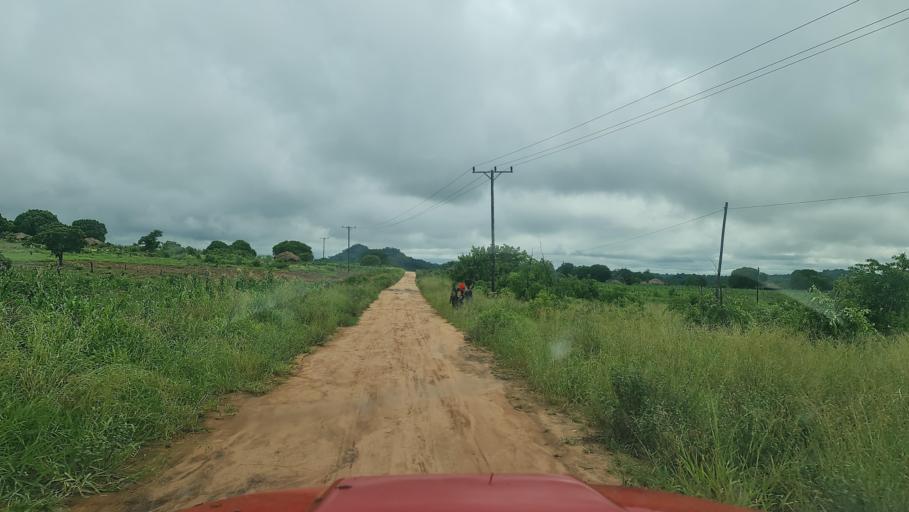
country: MW
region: Southern Region
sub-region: Nsanje District
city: Nsanje
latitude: -17.1844
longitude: 35.9260
